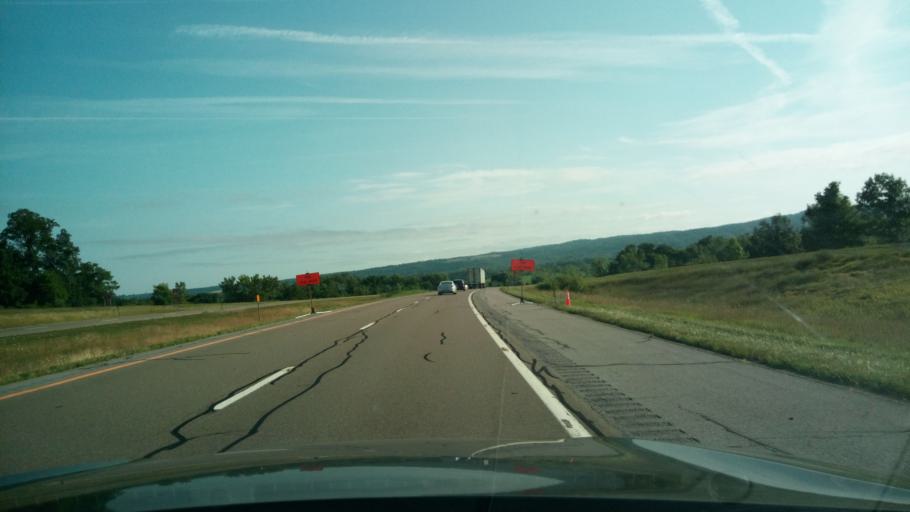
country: US
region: New York
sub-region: Livingston County
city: Mount Morris
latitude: 42.6719
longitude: -77.8113
